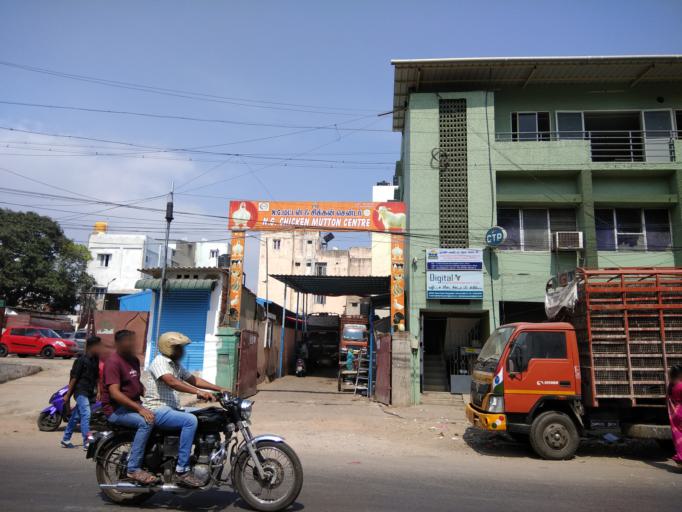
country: IN
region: Tamil Nadu
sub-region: Chennai
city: Chetput
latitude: 13.0535
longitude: 80.2681
